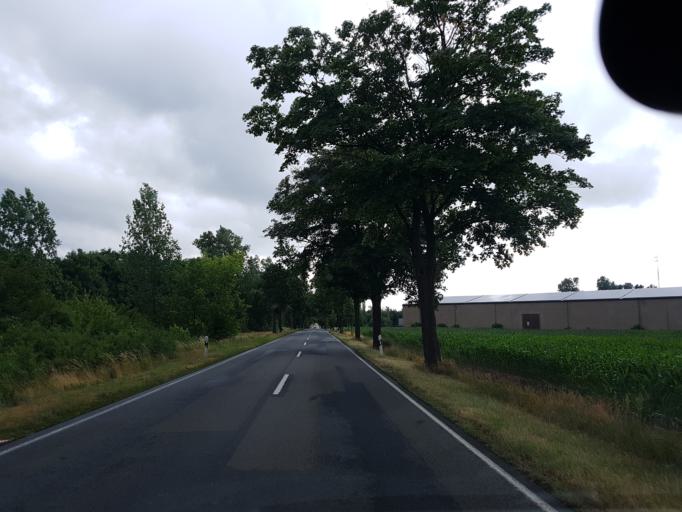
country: DE
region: Saxony-Anhalt
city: Seyda
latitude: 51.8872
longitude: 12.9236
